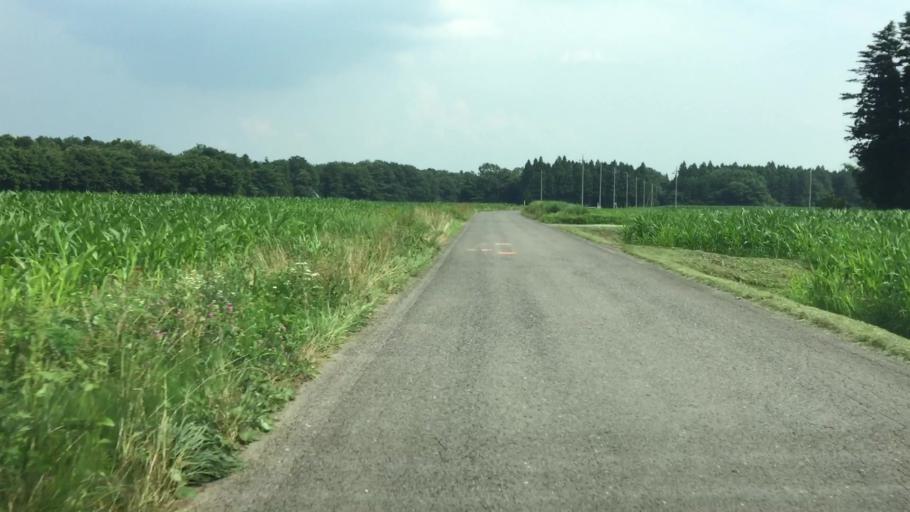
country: JP
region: Tochigi
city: Kuroiso
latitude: 37.0223
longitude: 139.9472
